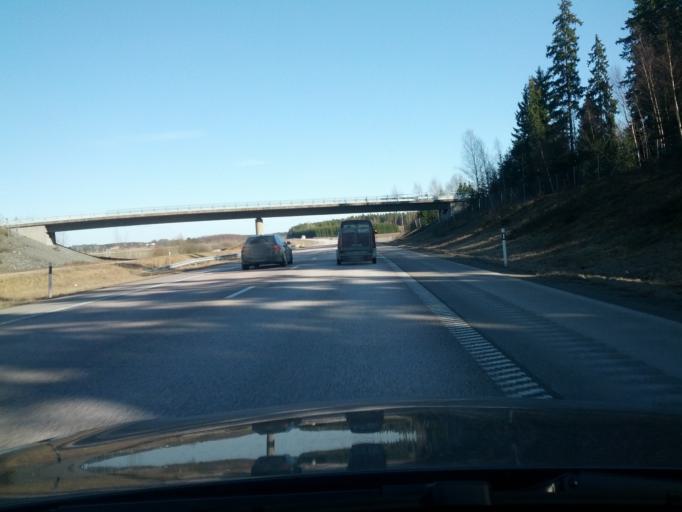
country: SE
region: Uppsala
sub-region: Enkopings Kommun
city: Grillby
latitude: 59.6403
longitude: 17.2219
